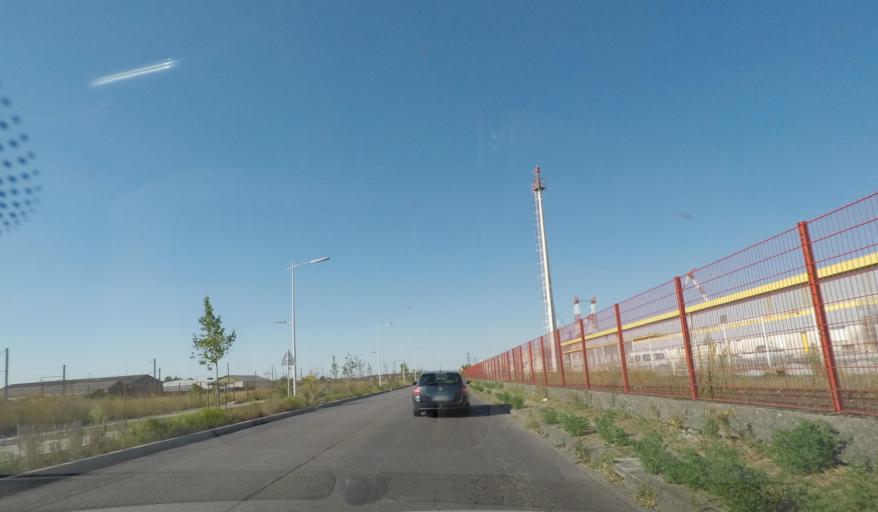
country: FR
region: Pays de la Loire
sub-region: Departement de la Loire-Atlantique
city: Saint-Nazaire
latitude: 47.2852
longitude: -2.2012
